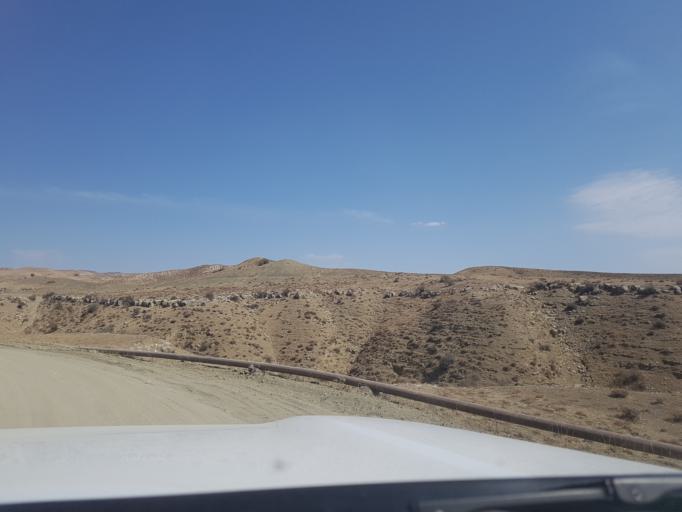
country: TM
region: Ahal
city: Baharly
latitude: 38.2430
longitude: 56.8903
